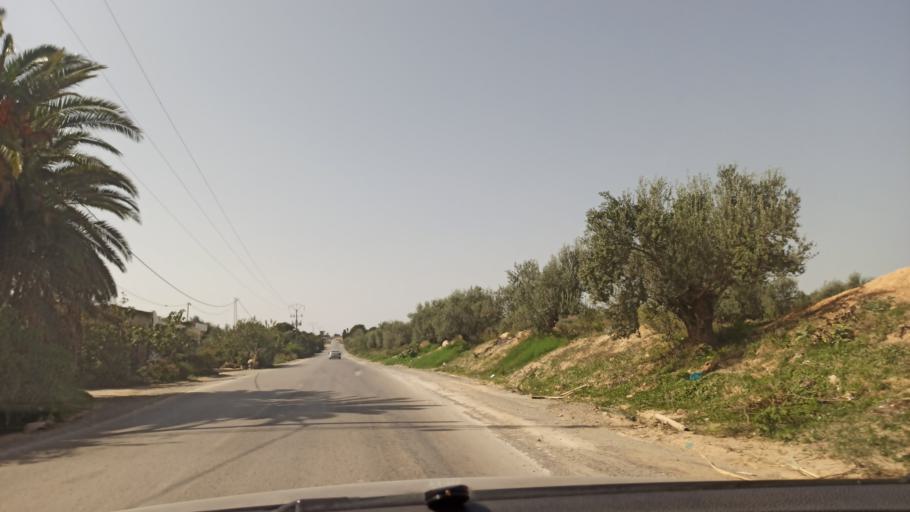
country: TN
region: Manouba
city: Manouba
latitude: 36.7449
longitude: 10.0937
